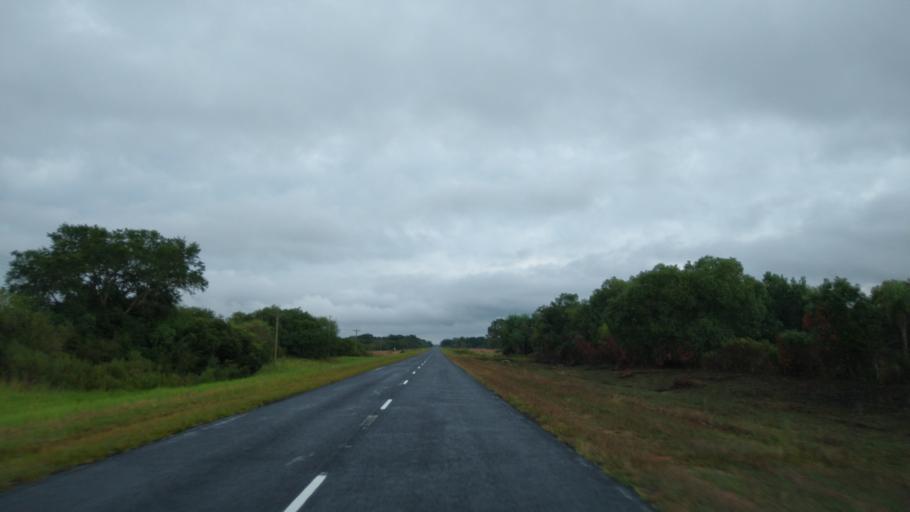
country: AR
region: Corrientes
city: Loreto
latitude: -27.7453
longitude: -57.2519
